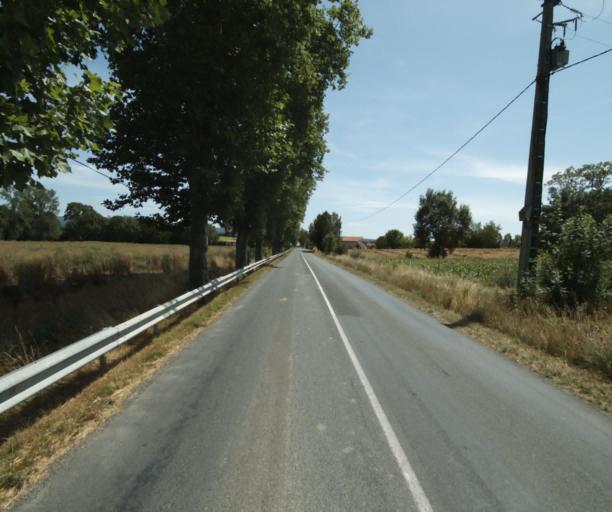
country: FR
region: Midi-Pyrenees
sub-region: Departement de la Haute-Garonne
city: Revel
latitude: 43.5138
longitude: 2.0102
